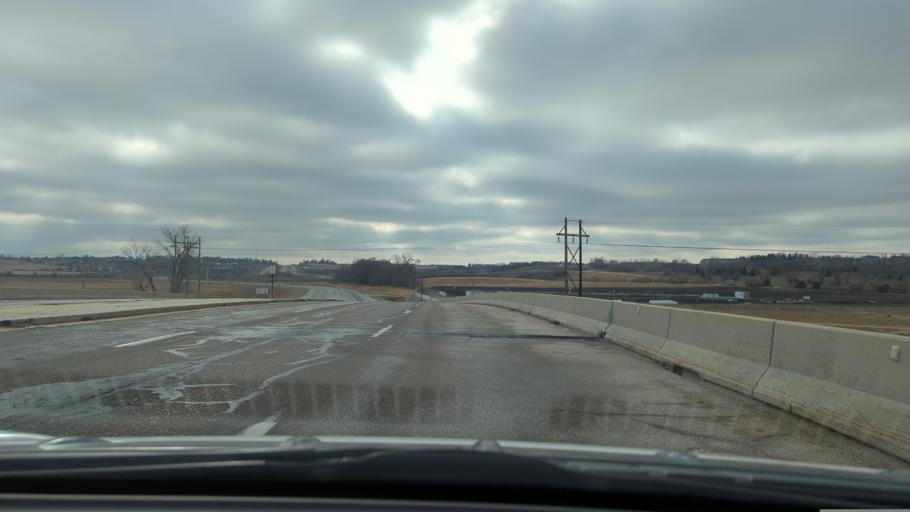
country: US
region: Nebraska
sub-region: Sarpy County
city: Offutt Air Force Base
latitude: 41.1123
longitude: -95.9278
